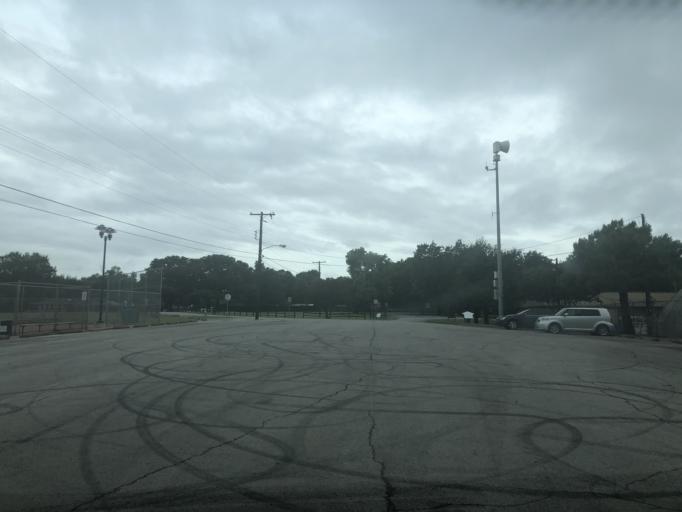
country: US
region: Texas
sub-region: Dallas County
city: Irving
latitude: 32.7973
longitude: -96.9414
